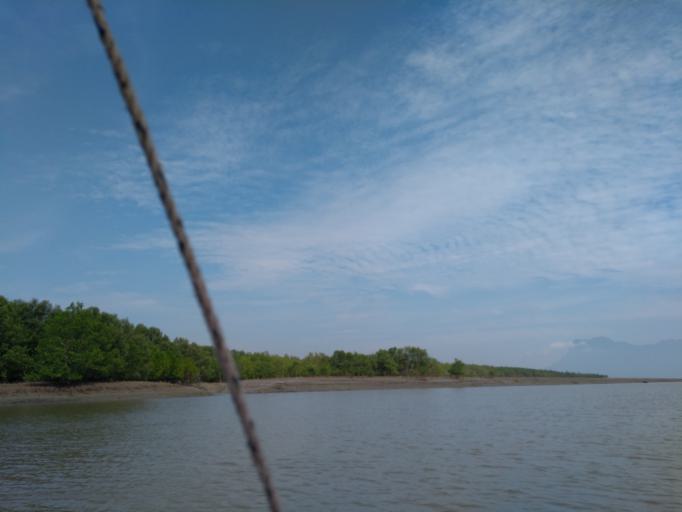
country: MY
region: Sarawak
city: Kuching
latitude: 1.6780
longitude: 110.4258
